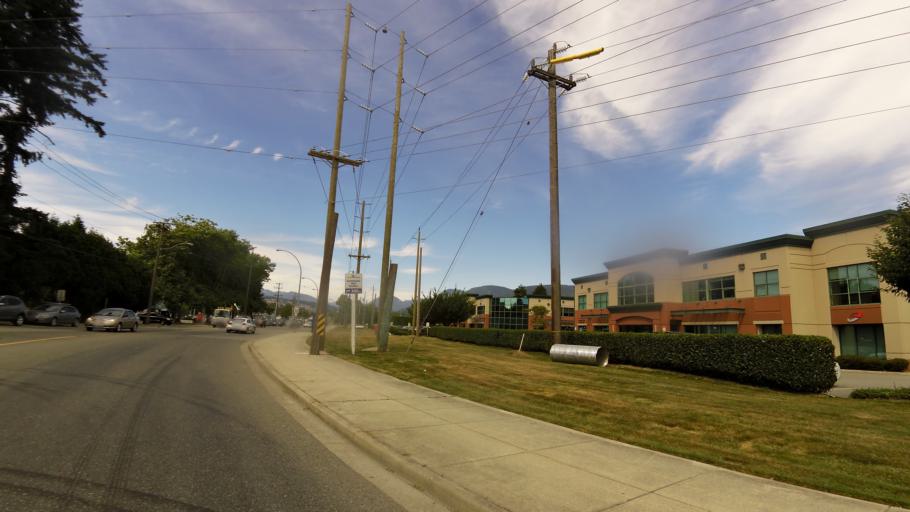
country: CA
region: British Columbia
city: Coquitlam
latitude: 49.2584
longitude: -122.7752
